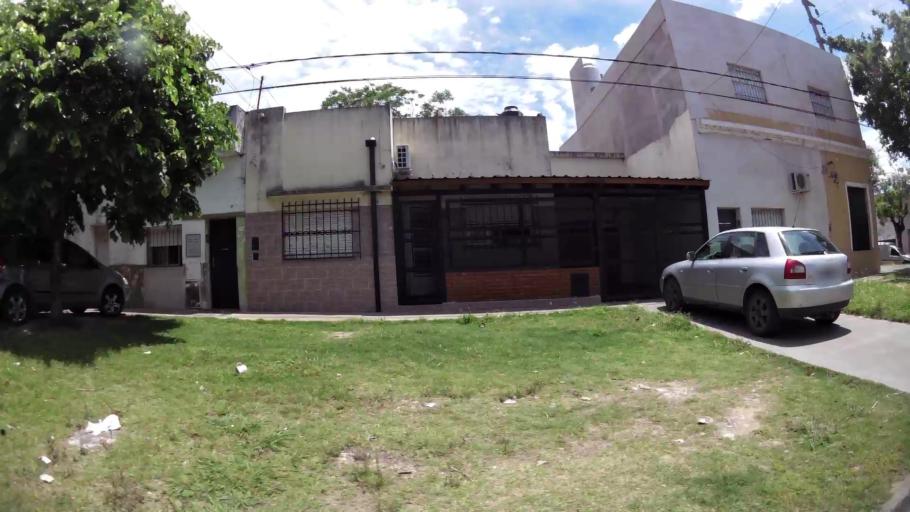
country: AR
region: Santa Fe
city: Gobernador Galvez
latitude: -33.0008
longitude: -60.6220
